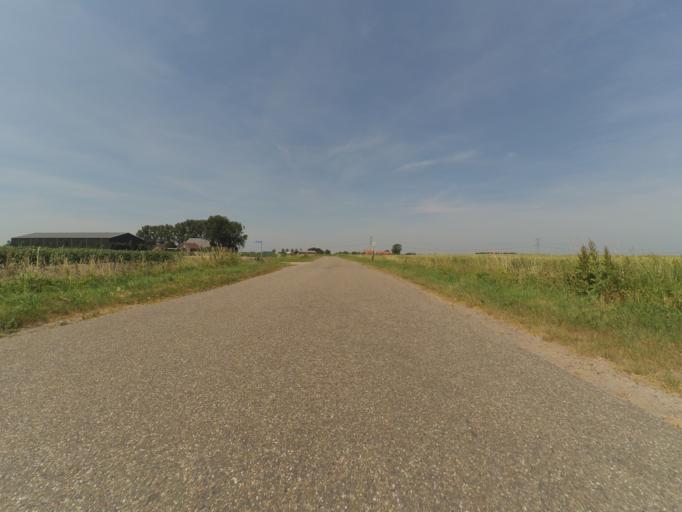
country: NL
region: North Brabant
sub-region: Gemeente Steenbergen
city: Kruisland
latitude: 51.5474
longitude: 4.3839
